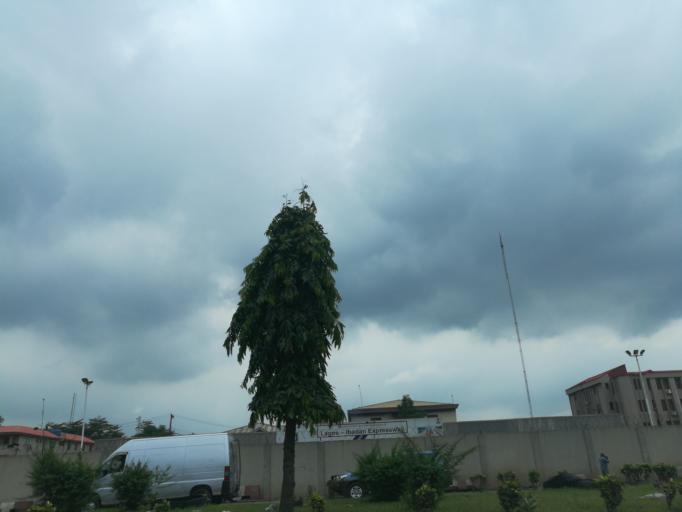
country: NG
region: Lagos
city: Ojota
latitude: 6.6035
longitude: 3.3751
